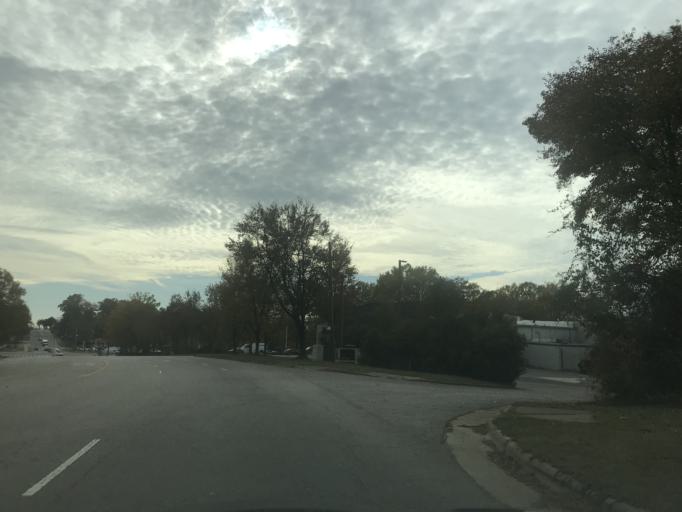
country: US
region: North Carolina
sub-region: Wake County
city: Raleigh
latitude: 35.8013
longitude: -78.5680
